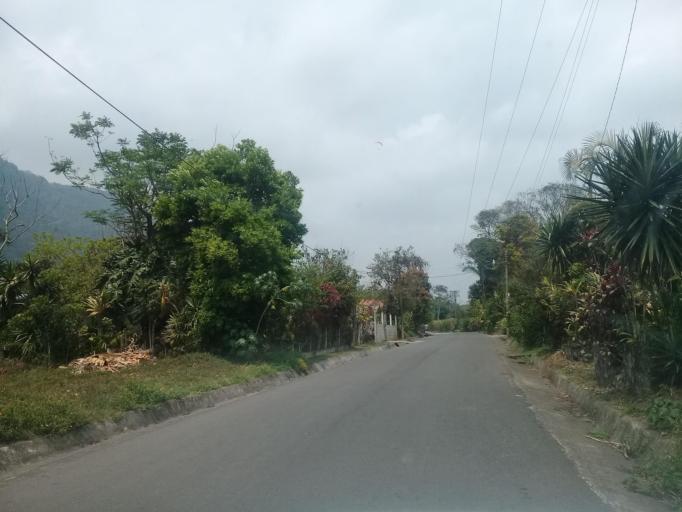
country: MX
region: Veracruz
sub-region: Cordoba
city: Fredepo
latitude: 18.8646
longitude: -96.9931
